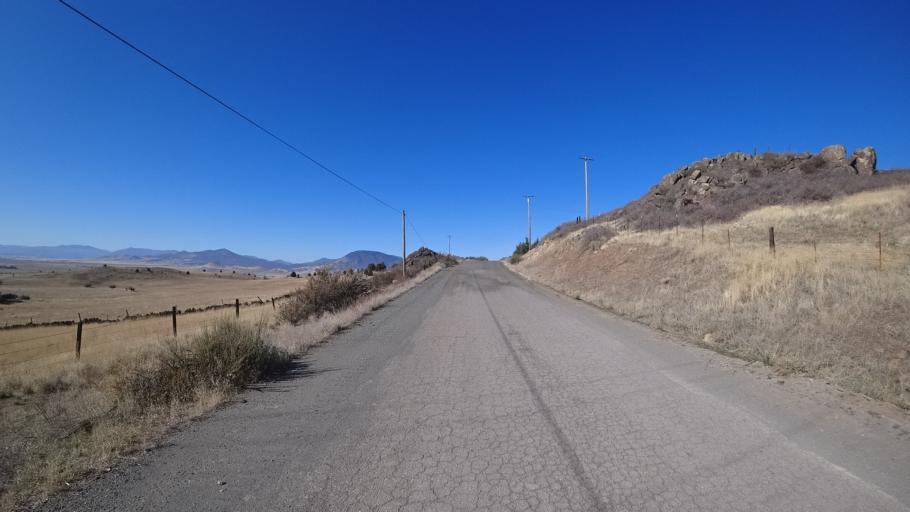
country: US
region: California
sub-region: Siskiyou County
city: Montague
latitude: 41.8309
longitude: -122.3715
